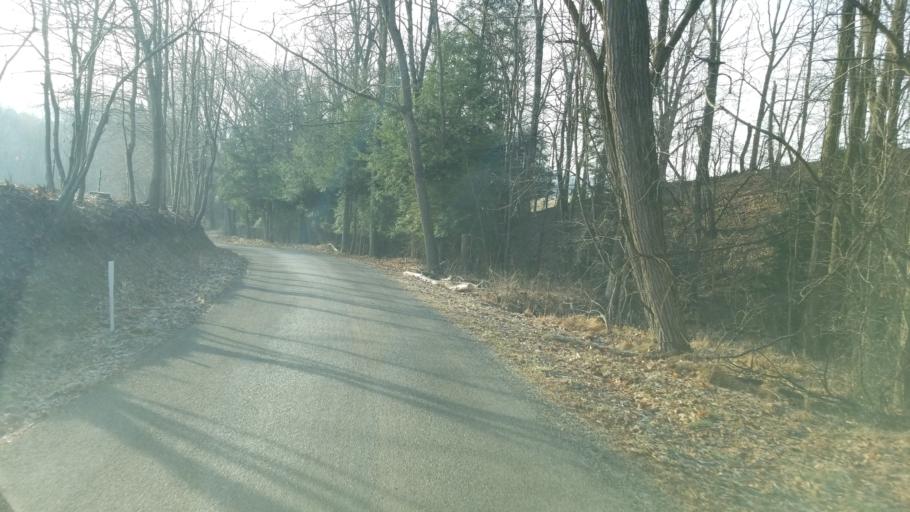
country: US
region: Pennsylvania
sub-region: Jefferson County
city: Brookville
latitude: 40.9577
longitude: -79.2642
